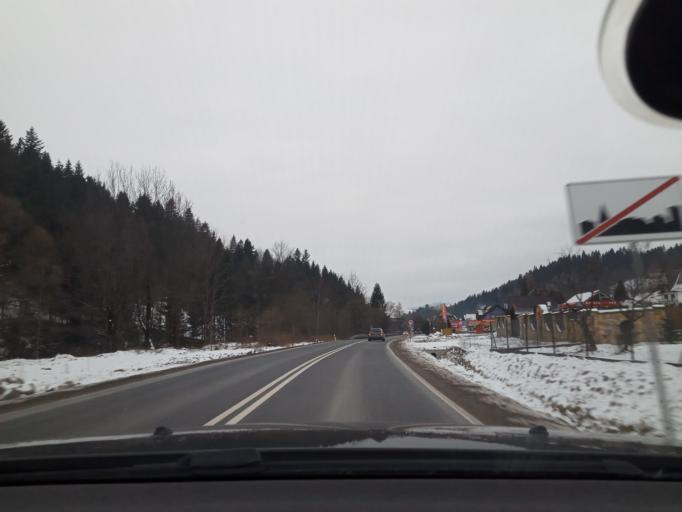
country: PL
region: Lesser Poland Voivodeship
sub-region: Powiat limanowski
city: Lubomierz
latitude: 49.6169
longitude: 20.1777
